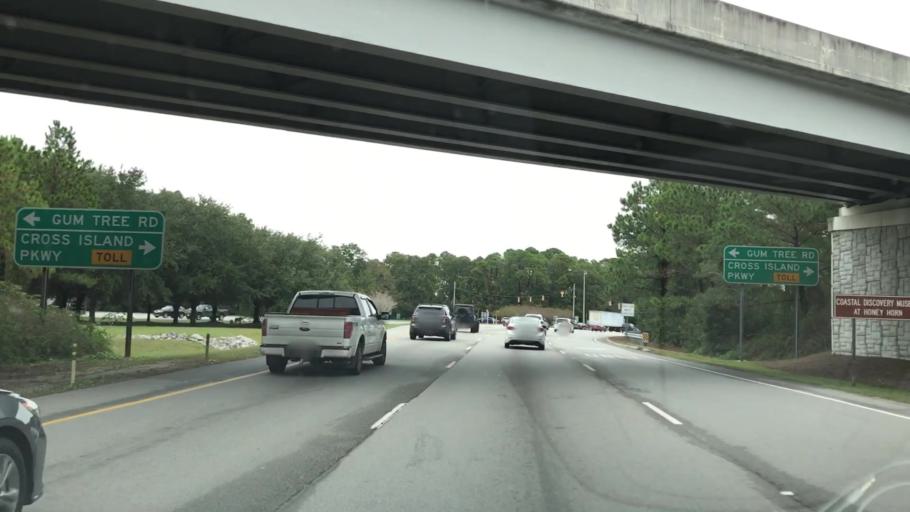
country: US
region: South Carolina
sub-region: Beaufort County
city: Hilton Head Island
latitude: 32.2155
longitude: -80.7399
